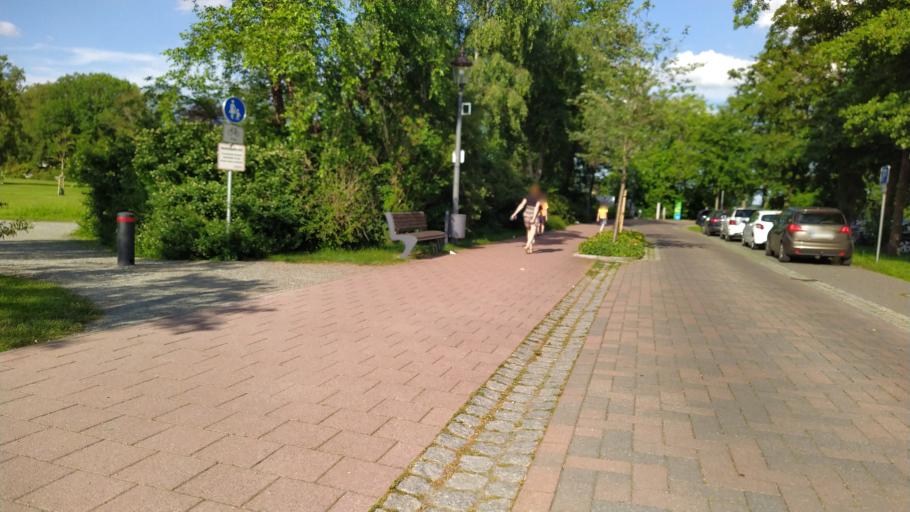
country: DE
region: Lower Saxony
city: Lintig
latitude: 53.6273
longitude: 8.8419
